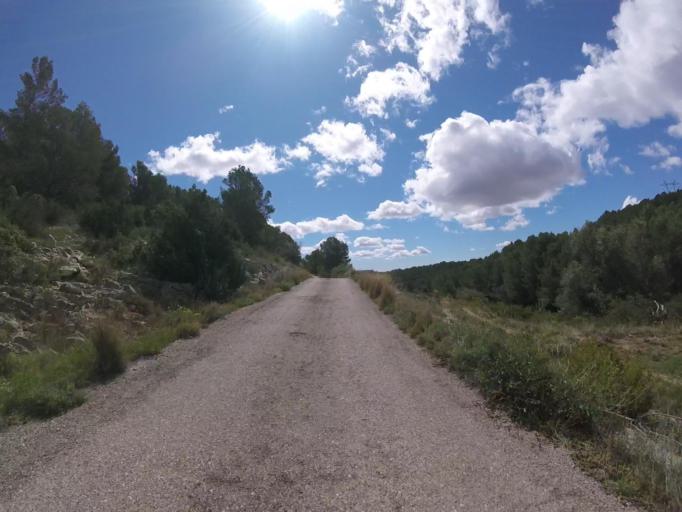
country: ES
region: Valencia
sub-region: Provincia de Castello
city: Adzaneta
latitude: 40.2701
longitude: -0.1065
